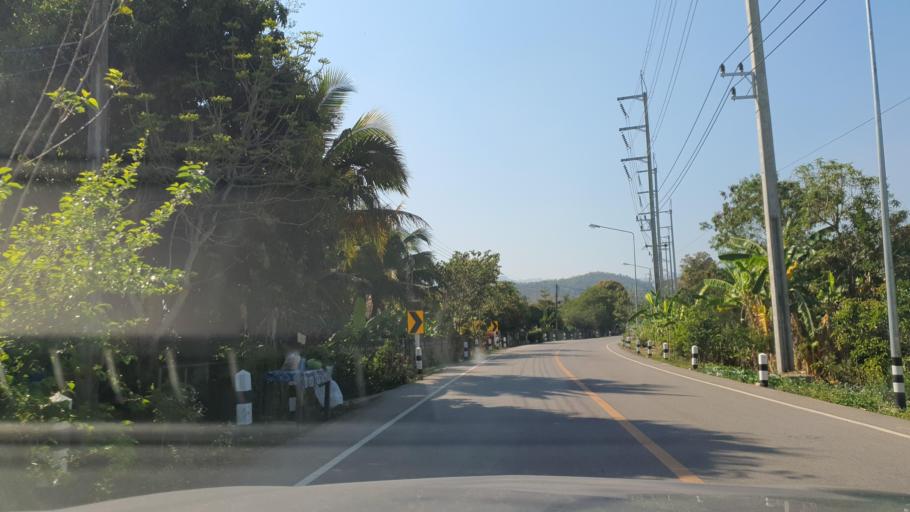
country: TH
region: Chiang Rai
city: Mae Lao
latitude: 19.8046
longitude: 99.6798
